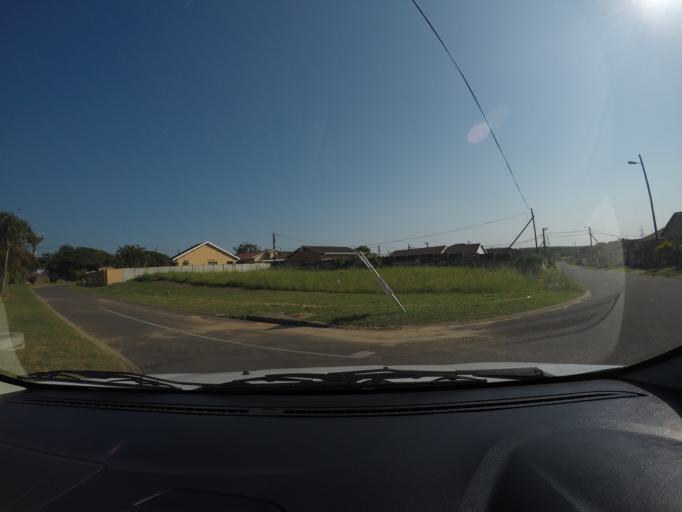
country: ZA
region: KwaZulu-Natal
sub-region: uThungulu District Municipality
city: Richards Bay
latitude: -28.7210
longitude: 32.0392
